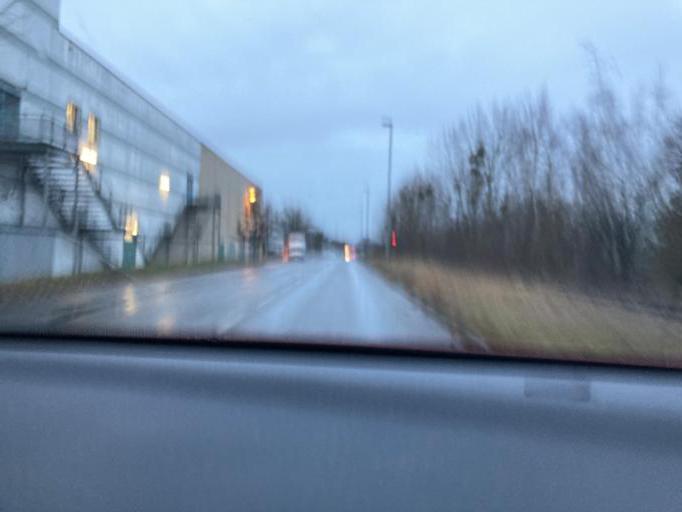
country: DE
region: Saxony-Anhalt
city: Naumburg
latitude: 51.1471
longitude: 11.8330
